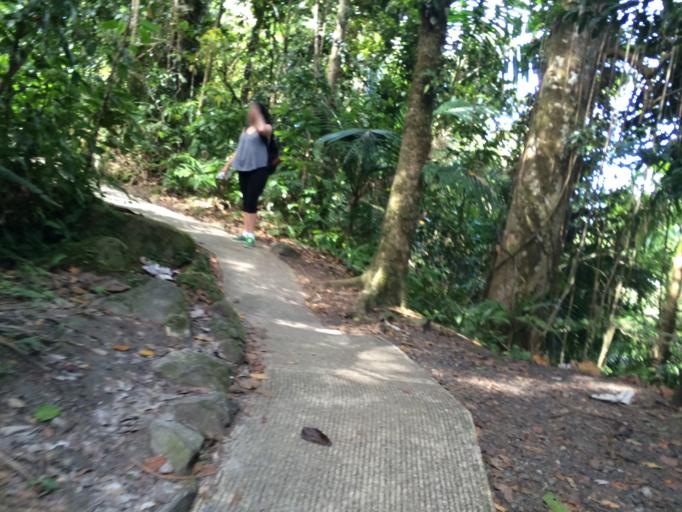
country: PR
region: Rio Grande
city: Palmer
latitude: 18.3081
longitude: -65.7750
